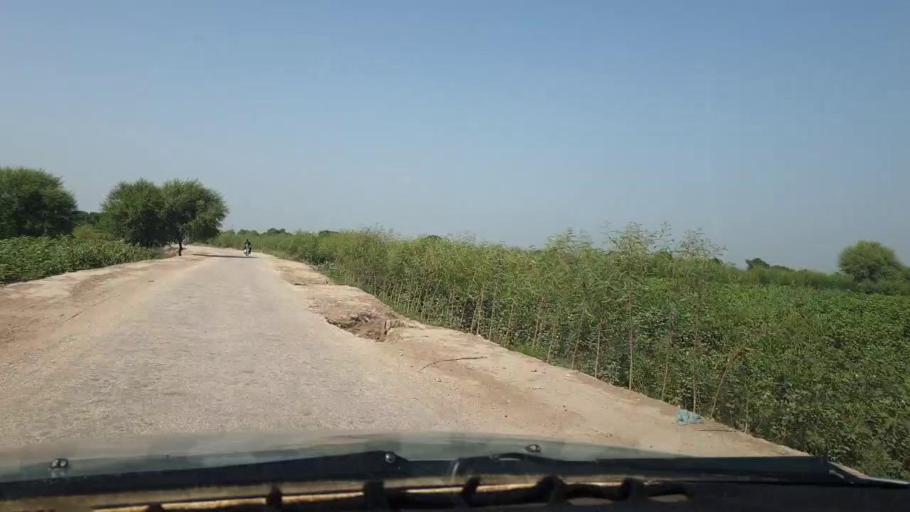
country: PK
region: Sindh
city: Chambar
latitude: 25.2243
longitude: 68.8706
